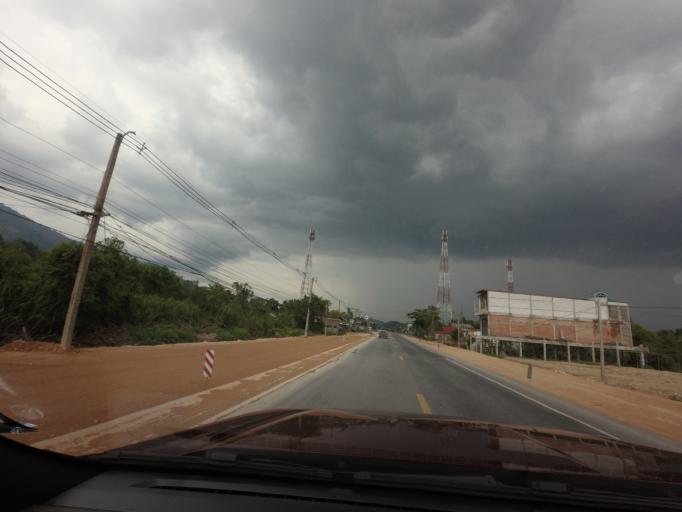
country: TH
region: Yala
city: Krong Pi Nang
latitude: 6.4227
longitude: 101.2784
